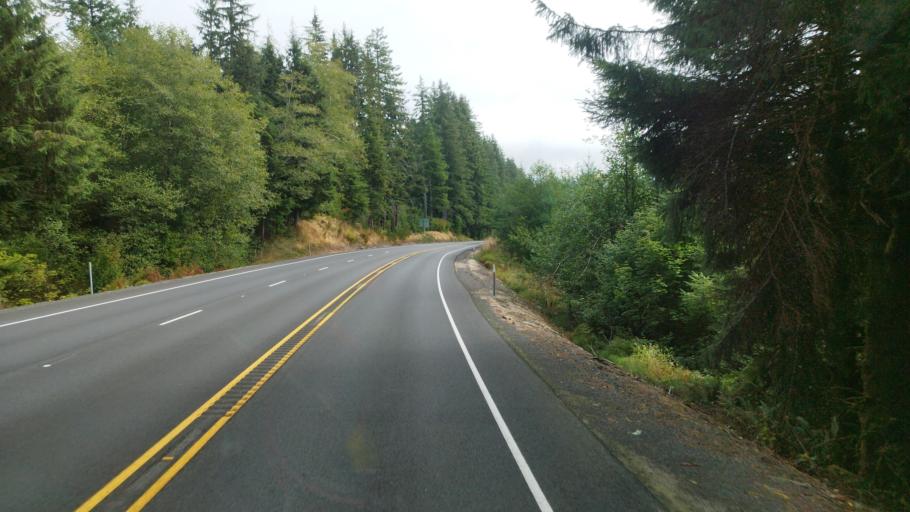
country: US
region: Oregon
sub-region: Clatsop County
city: Seaside
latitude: 45.9028
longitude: -123.6646
